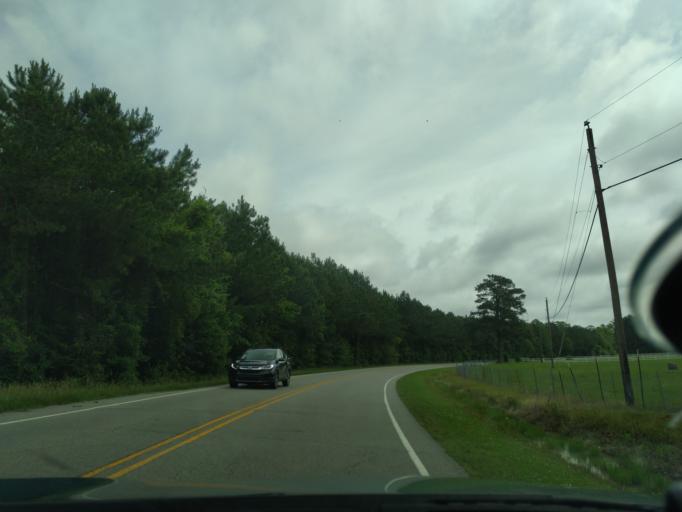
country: US
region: North Carolina
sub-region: Washington County
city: Plymouth
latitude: 35.9042
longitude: -76.6092
